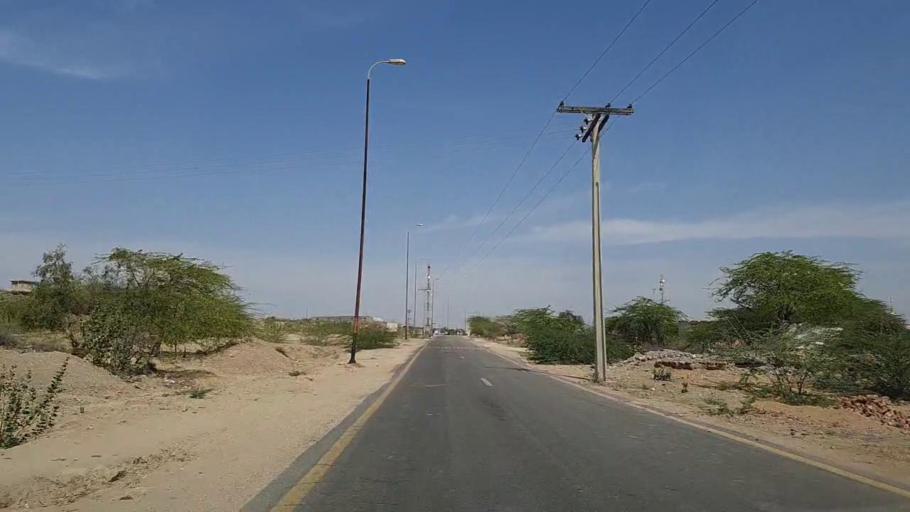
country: PK
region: Sindh
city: Mithi
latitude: 24.9726
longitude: 69.9154
